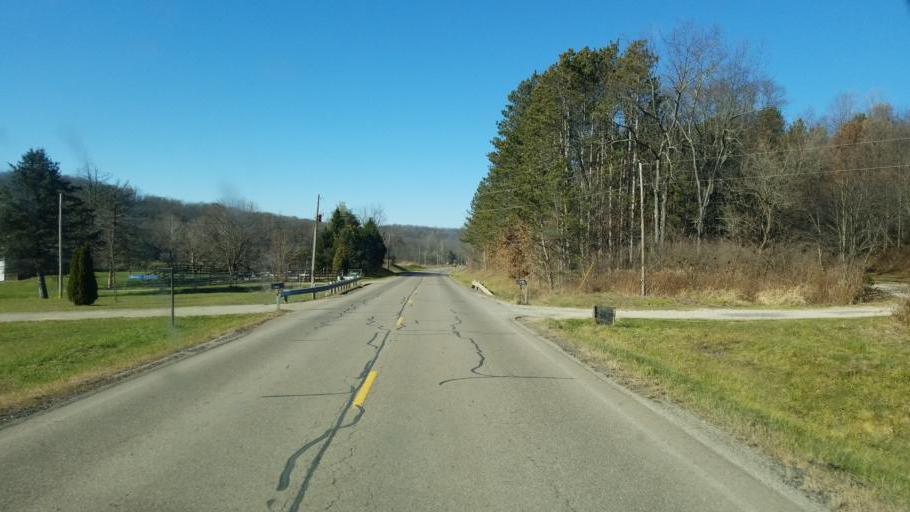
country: US
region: Ohio
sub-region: Knox County
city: Oak Hill
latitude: 40.3575
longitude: -82.2298
